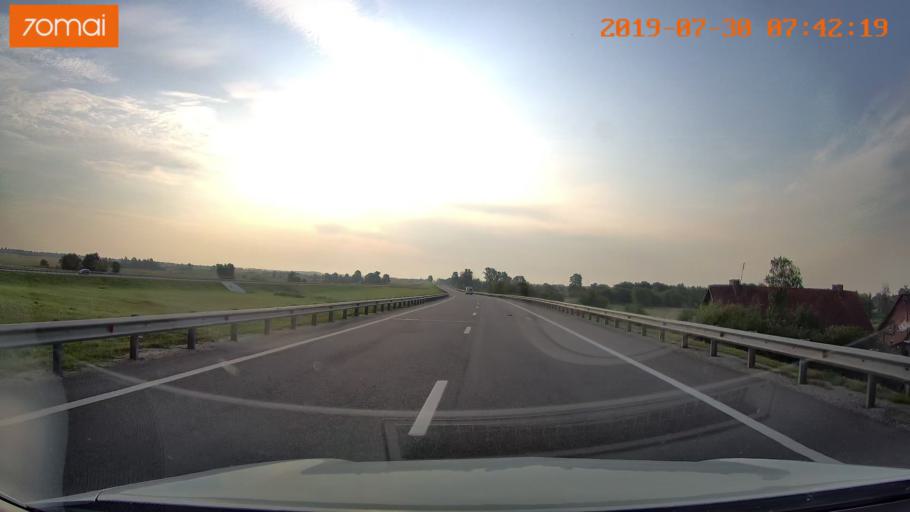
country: RU
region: Kaliningrad
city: Gvardeysk
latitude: 54.6477
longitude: 21.2754
